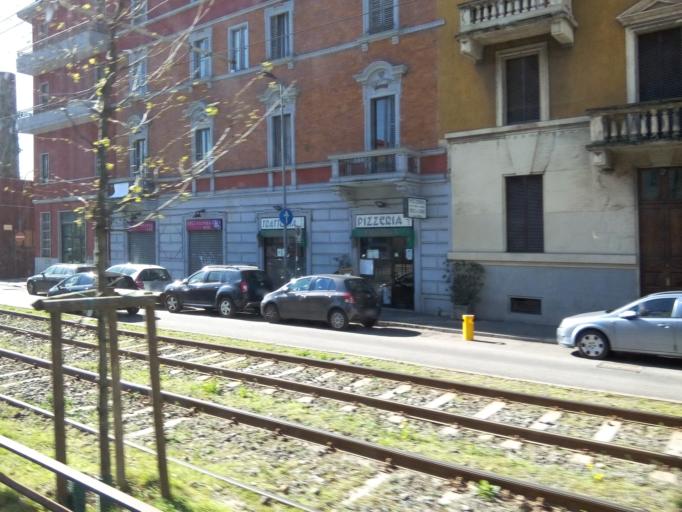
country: IT
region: Lombardy
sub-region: Citta metropolitana di Milano
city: Novate Milanese
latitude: 45.4979
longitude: 9.1342
